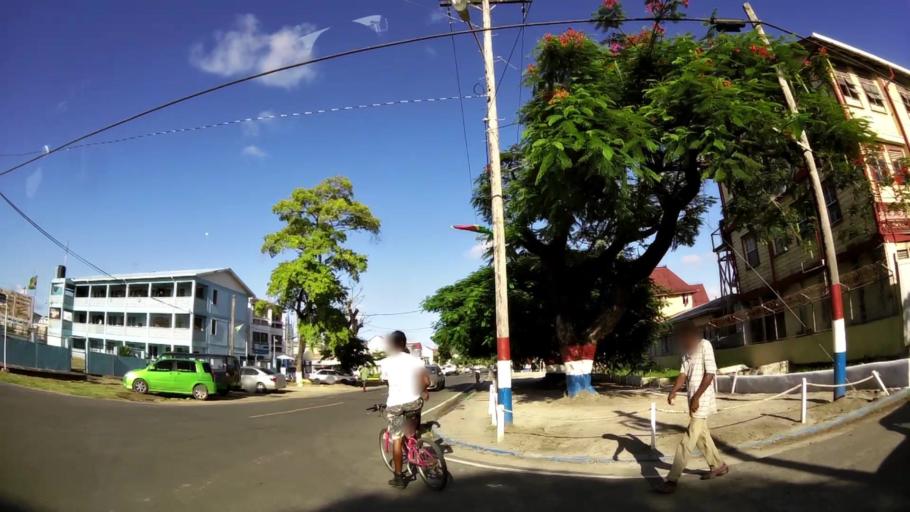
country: GY
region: Demerara-Mahaica
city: Georgetown
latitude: 6.8085
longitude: -58.1645
